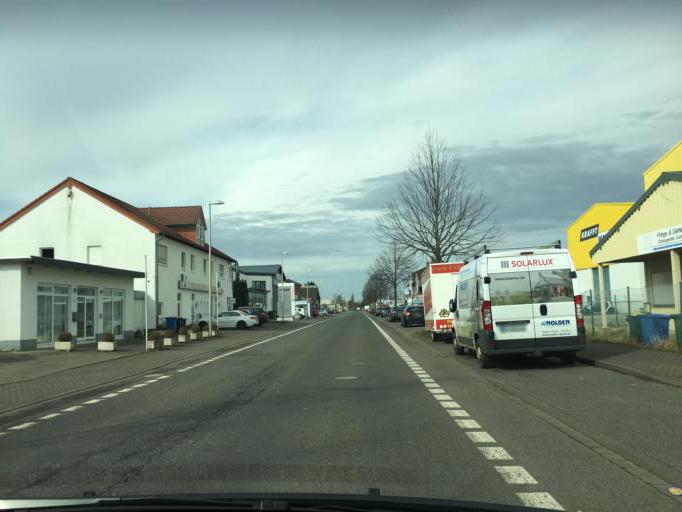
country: DE
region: North Rhine-Westphalia
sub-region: Regierungsbezirk Koln
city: Dueren
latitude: 50.8144
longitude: 6.5078
